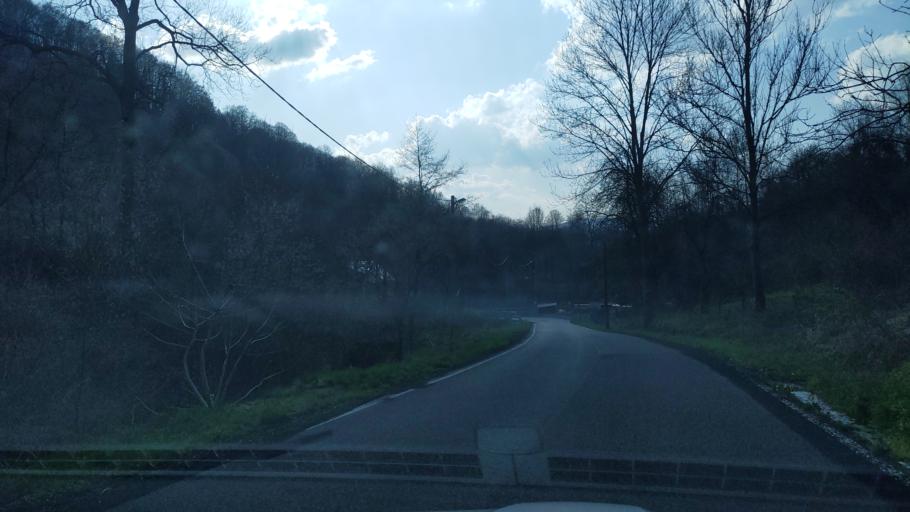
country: CZ
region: Ustecky
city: Povrly
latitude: 50.7053
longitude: 14.2249
